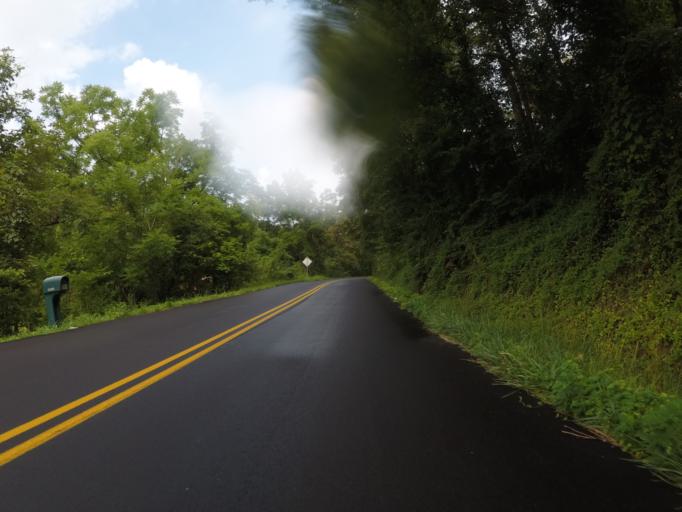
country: US
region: Kentucky
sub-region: Boyd County
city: Meads
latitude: 38.4003
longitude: -82.6560
